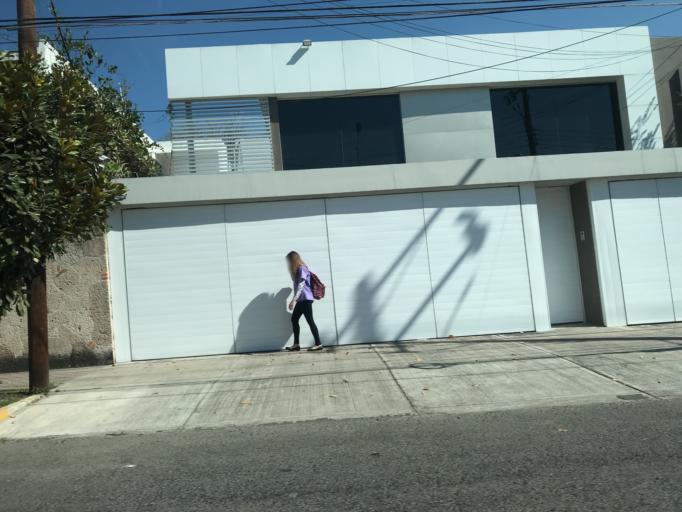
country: MX
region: Jalisco
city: Guadalajara
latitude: 20.6689
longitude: -103.3773
